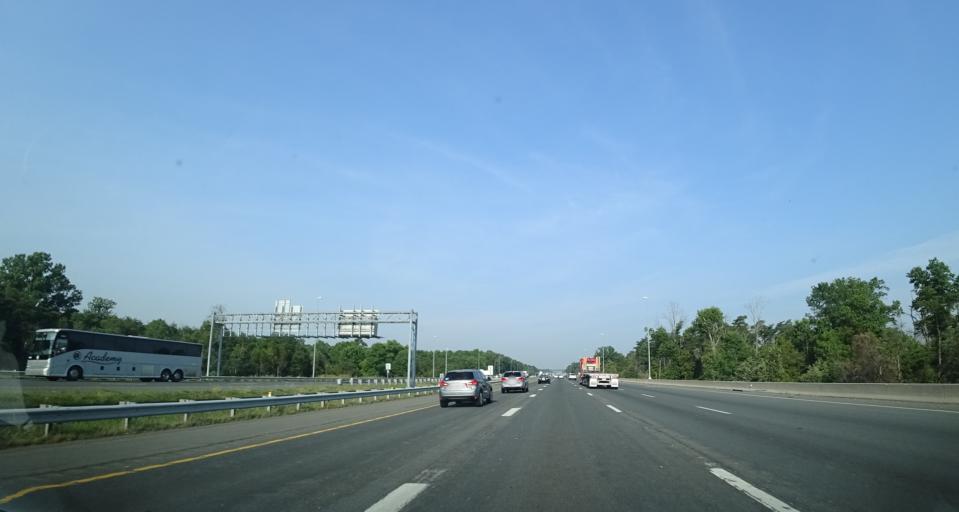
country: US
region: Virginia
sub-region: Prince William County
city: Bull Run
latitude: 38.8008
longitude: -77.5308
